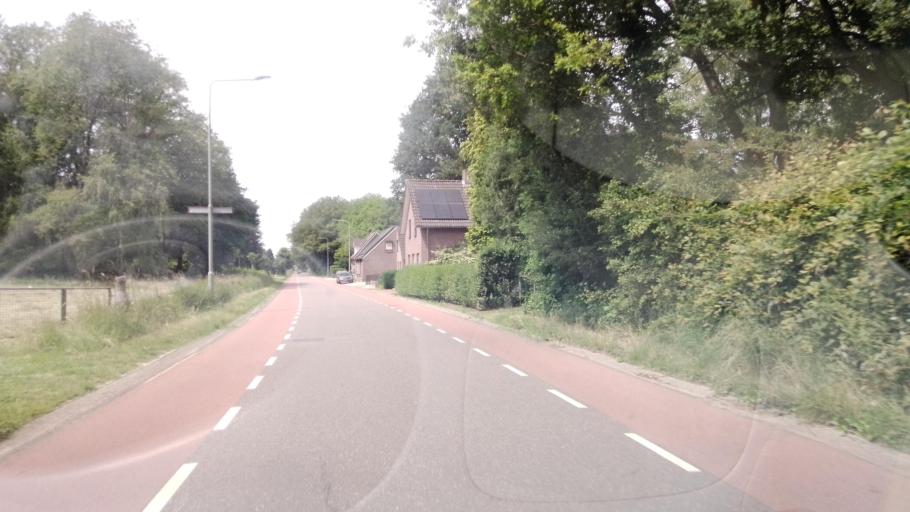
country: NL
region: North Brabant
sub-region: Gemeente Boxmeer
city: Boxmeer
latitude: 51.6342
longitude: 6.0284
